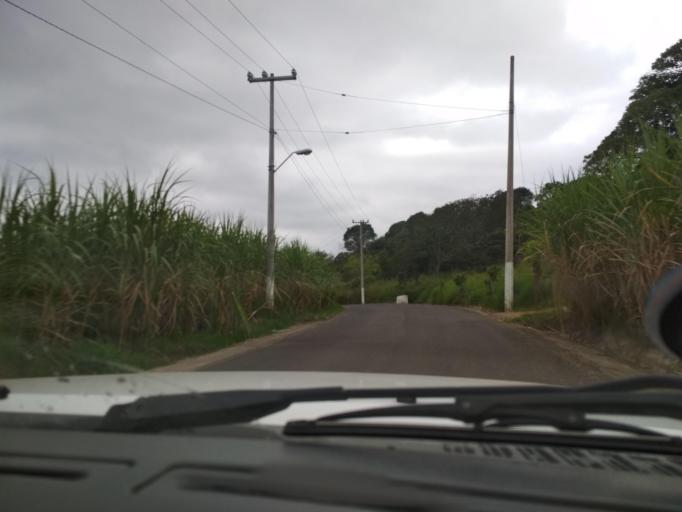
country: MX
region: Veracruz
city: El Castillo
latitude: 19.5660
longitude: -96.8456
